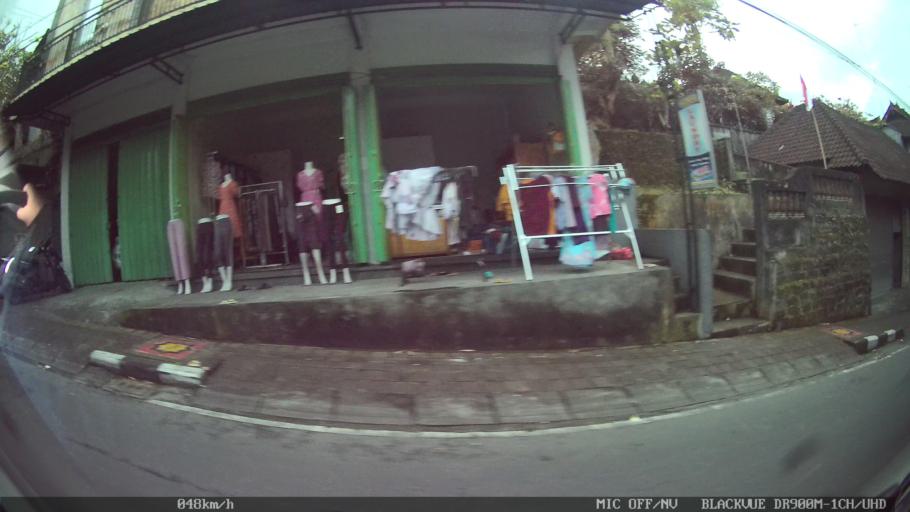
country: ID
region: Bali
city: Banjar Pekenjelodan
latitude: -8.5649
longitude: 115.1755
